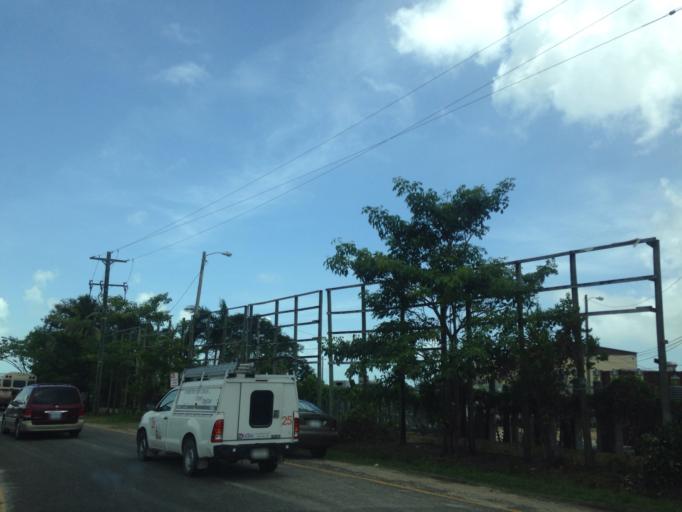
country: BZ
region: Belize
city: Belize City
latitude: 17.5356
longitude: -88.3073
